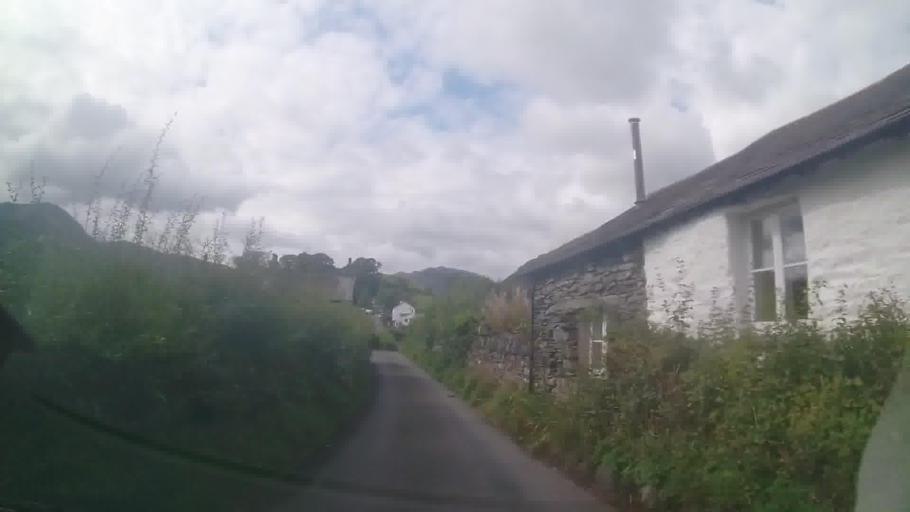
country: GB
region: England
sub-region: Cumbria
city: Ambleside
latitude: 54.4212
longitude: -3.0524
